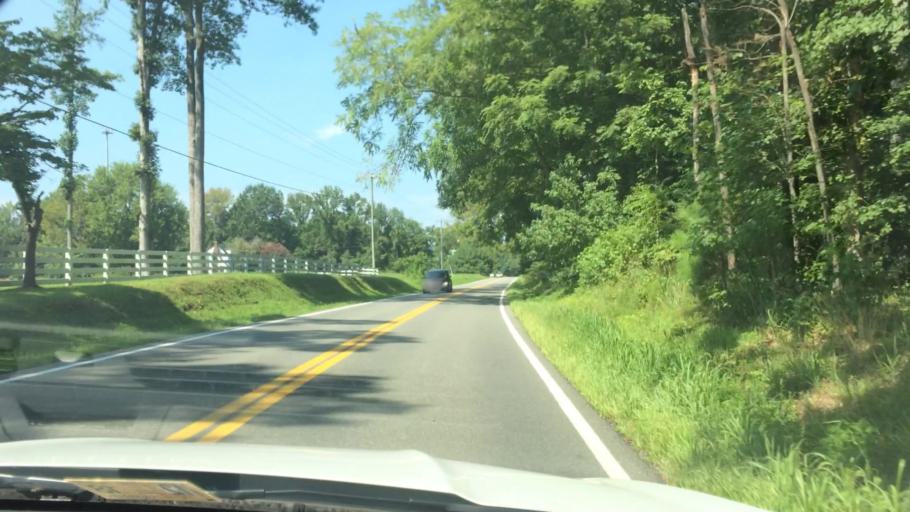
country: US
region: Virginia
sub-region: New Kent County
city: New Kent
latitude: 37.5234
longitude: -77.0583
